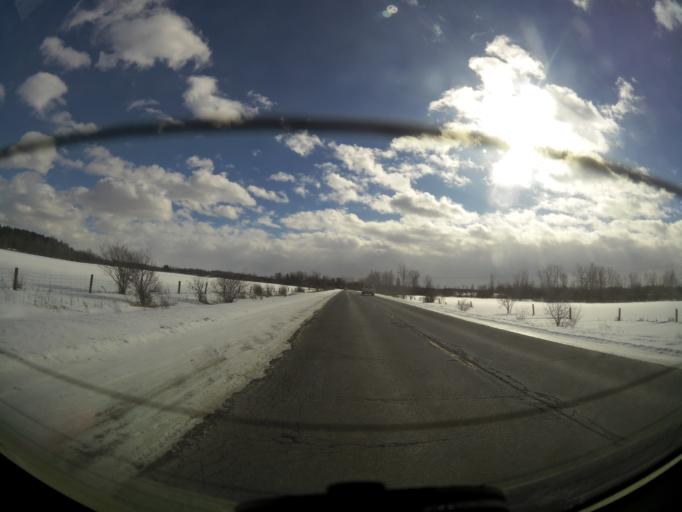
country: CA
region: Ontario
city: Ottawa
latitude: 45.3824
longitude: -75.5744
